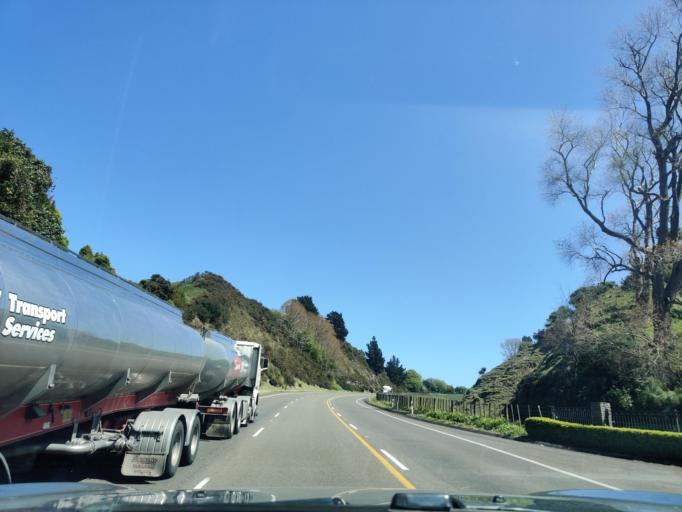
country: NZ
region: Manawatu-Wanganui
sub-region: Wanganui District
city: Wanganui
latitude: -39.8258
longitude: 174.8793
